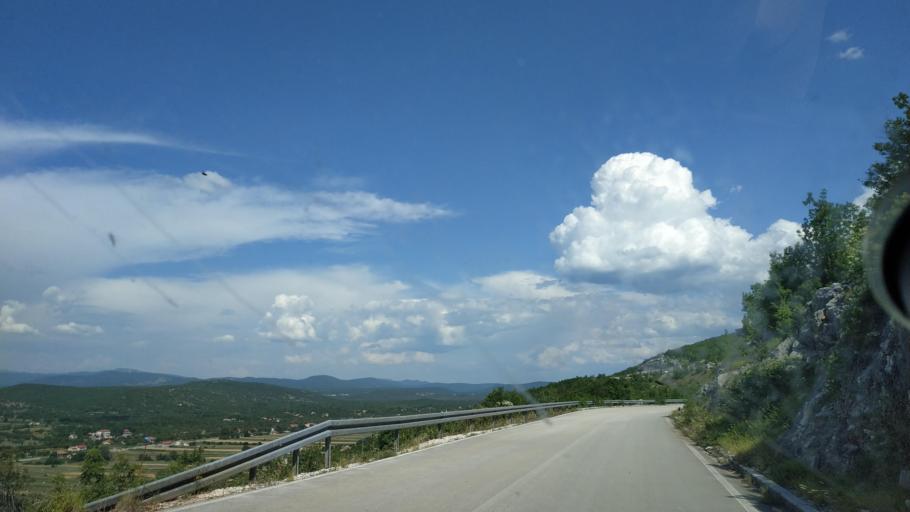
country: HR
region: Splitsko-Dalmatinska
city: Dugopolje
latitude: 43.5842
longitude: 16.6521
